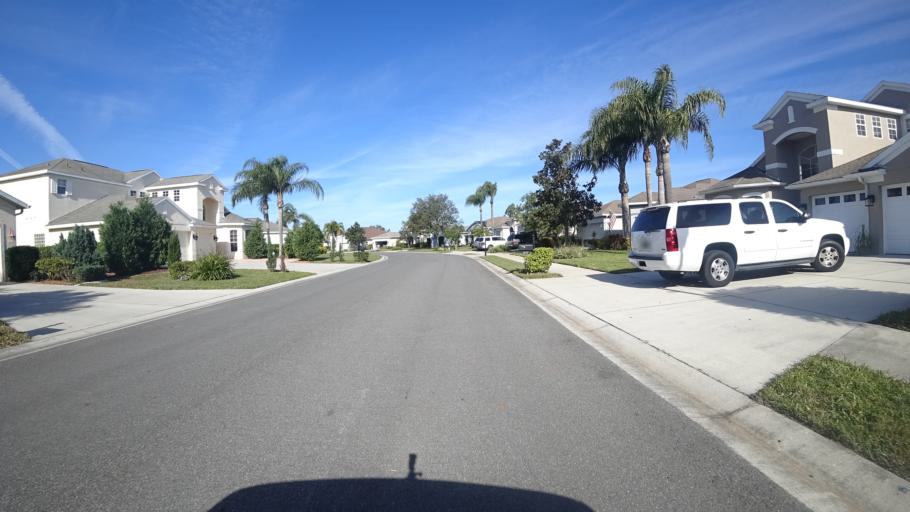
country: US
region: Florida
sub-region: Manatee County
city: Bayshore Gardens
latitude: 27.4493
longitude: -82.6168
